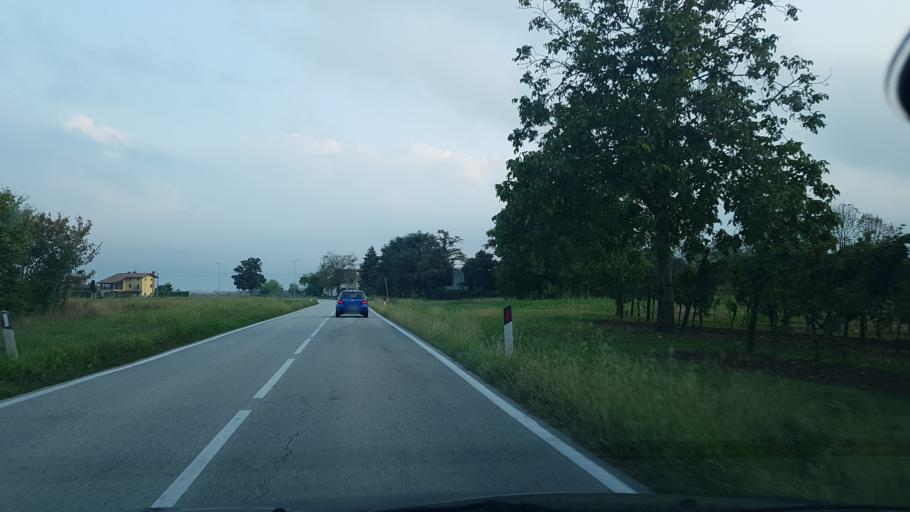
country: IT
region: Friuli Venezia Giulia
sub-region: Provincia di Udine
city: Trivignano Udinese
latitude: 45.9435
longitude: 13.3481
